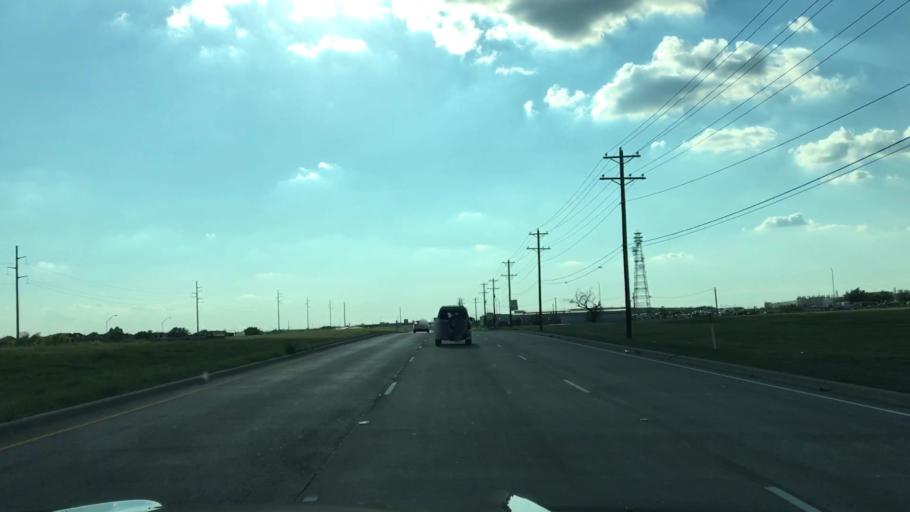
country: US
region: Texas
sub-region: Denton County
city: Justin
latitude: 33.0270
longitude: -97.2908
